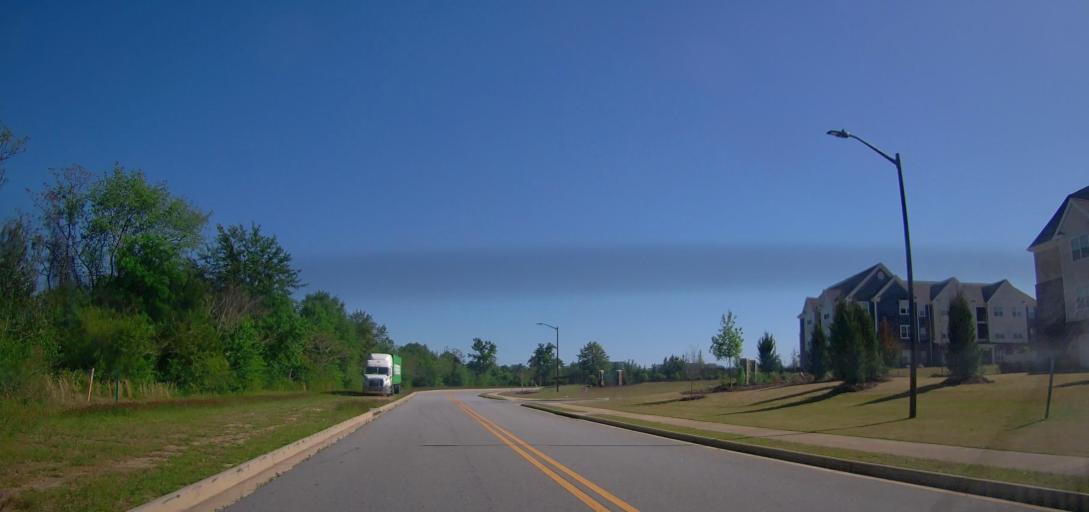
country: US
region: Georgia
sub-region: Houston County
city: Robins Air Force Base
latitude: 32.6038
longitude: -83.5949
